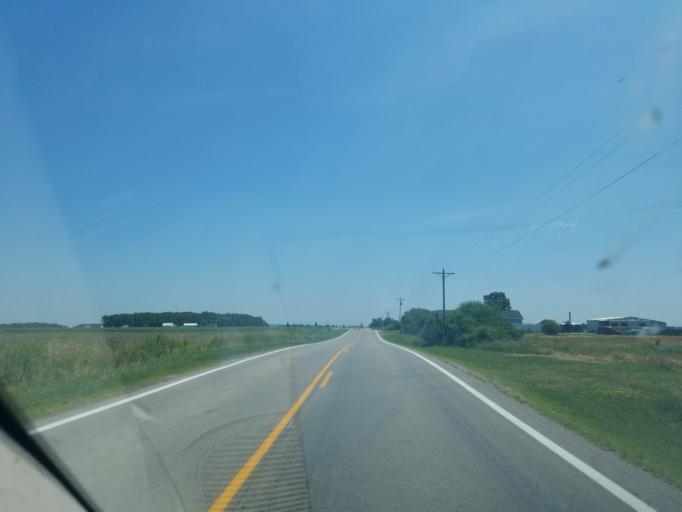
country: US
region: Ohio
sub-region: Mercer County
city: Rockford
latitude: 40.7423
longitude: -84.6975
